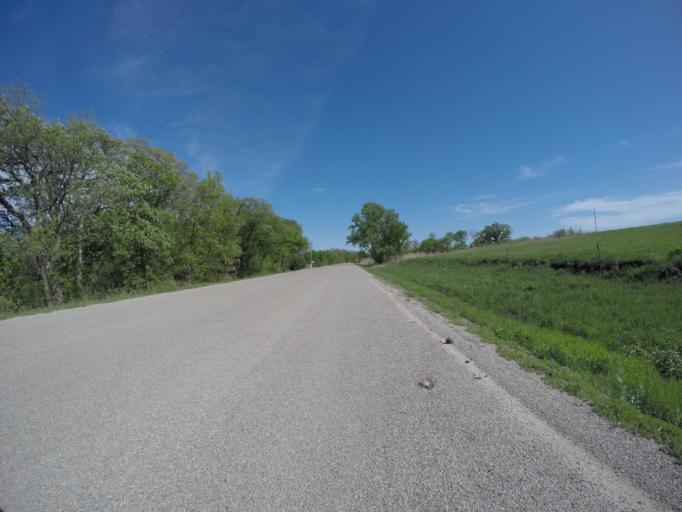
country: US
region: Kansas
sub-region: Riley County
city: Ogden
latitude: 39.0015
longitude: -96.5996
